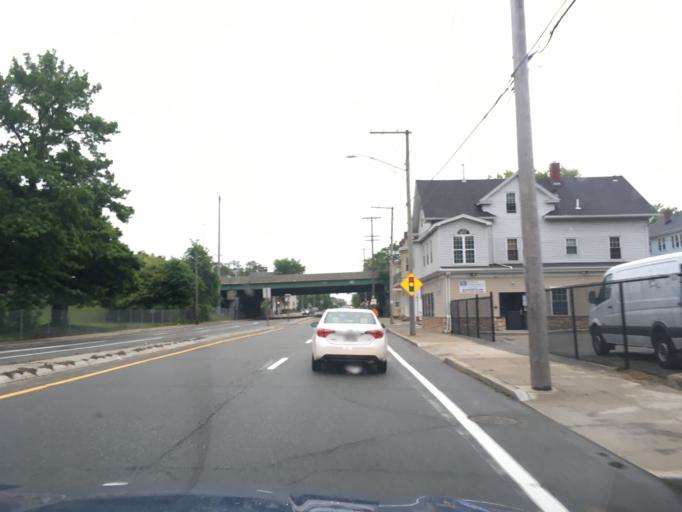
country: US
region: Rhode Island
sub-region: Providence County
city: Cranston
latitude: 41.7827
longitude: -71.4194
